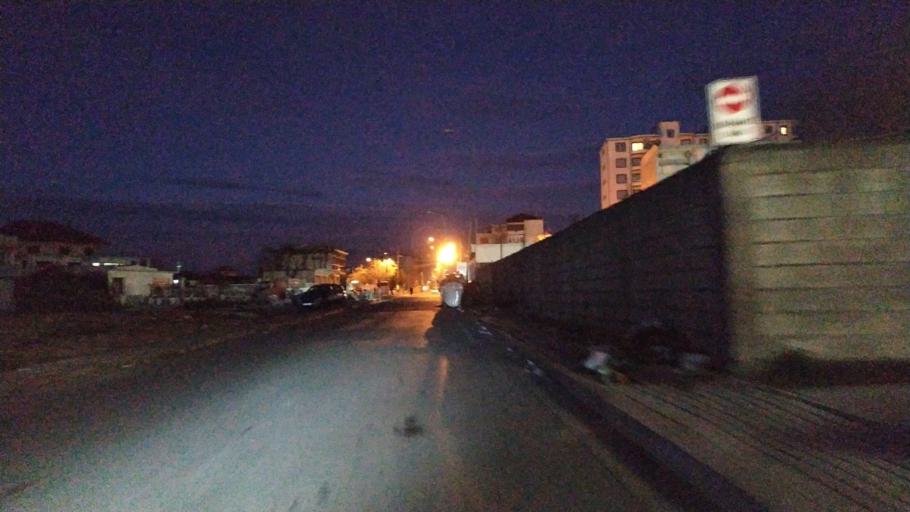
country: AL
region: Shkoder
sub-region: Rrethi i Shkodres
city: Shkoder
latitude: 42.0567
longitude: 19.4999
